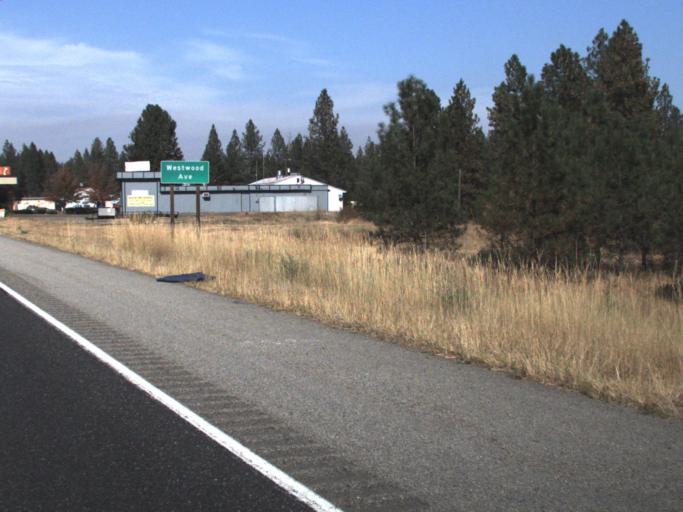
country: US
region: Washington
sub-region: Spokane County
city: Deer Park
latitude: 47.9124
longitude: -117.3502
